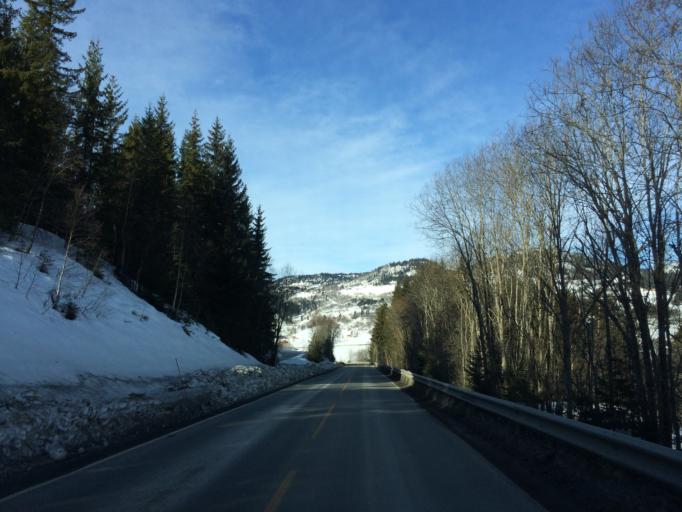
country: NO
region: Oppland
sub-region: Gausdal
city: Segalstad bru
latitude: 61.2782
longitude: 10.1605
